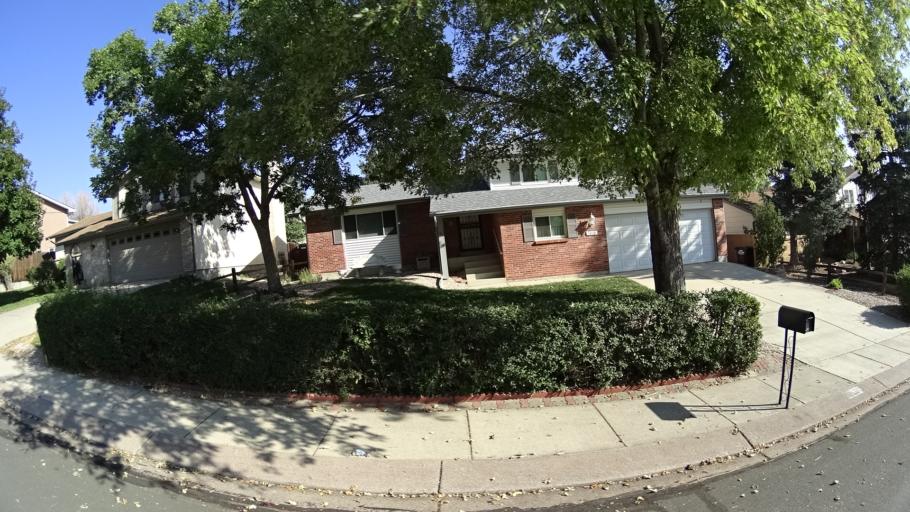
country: US
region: Colorado
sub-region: El Paso County
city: Cimarron Hills
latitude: 38.8811
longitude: -104.7258
